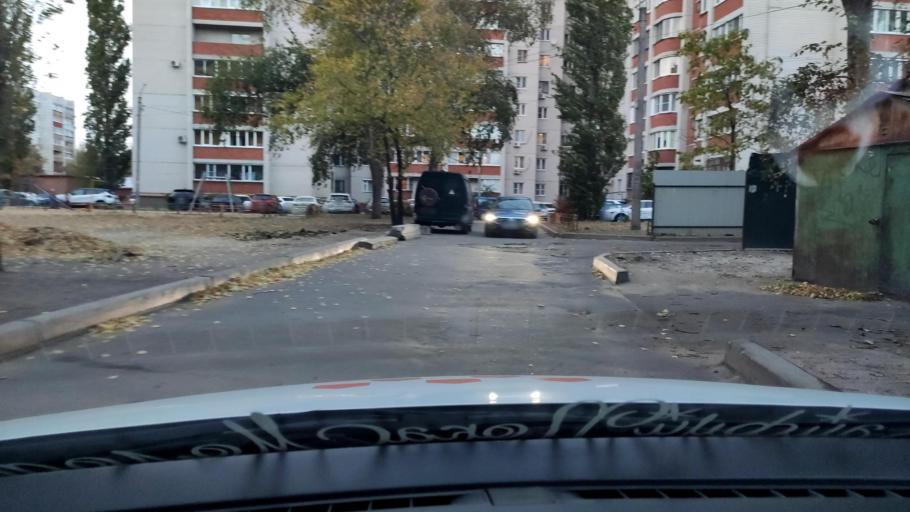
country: RU
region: Voronezj
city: Podgornoye
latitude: 51.6995
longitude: 39.1432
